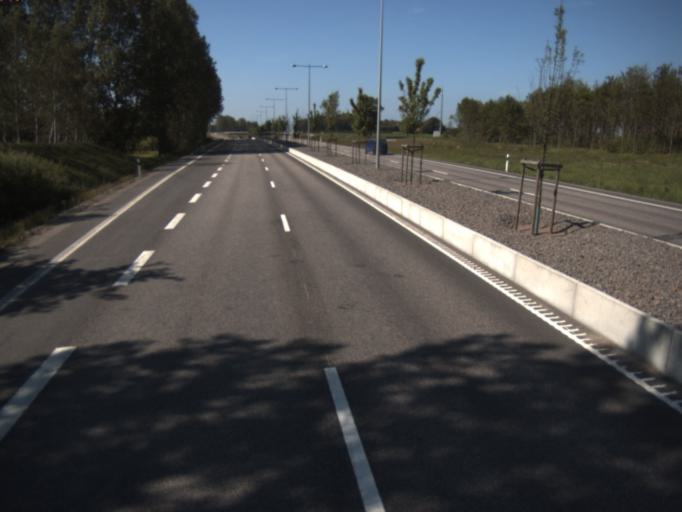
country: SE
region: Skane
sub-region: Helsingborg
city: Odakra
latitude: 56.0493
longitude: 12.7542
